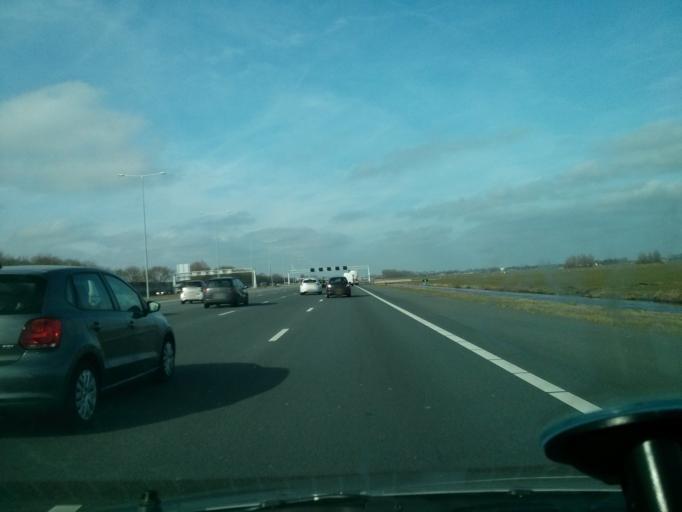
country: NL
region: Utrecht
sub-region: Stichtse Vecht
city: Vreeland
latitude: 52.2360
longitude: 4.9769
